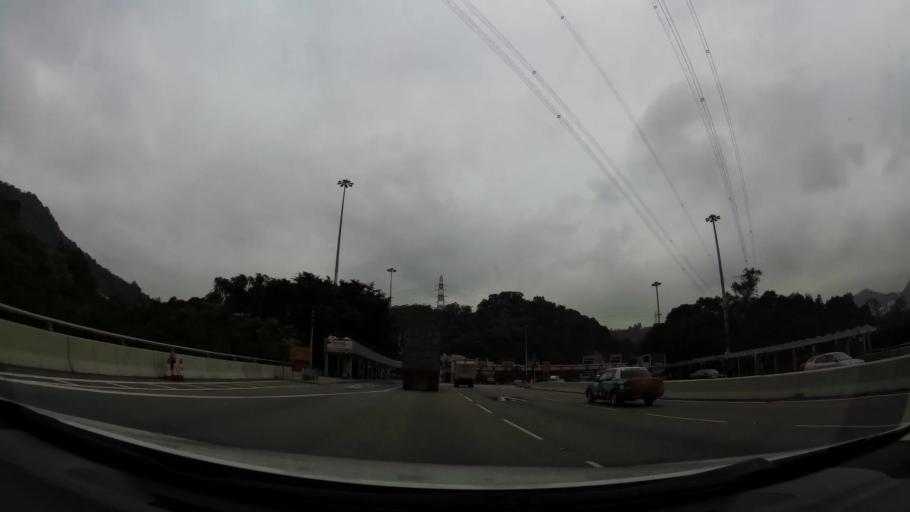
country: HK
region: Tsuen Wan
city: Tsuen Wan
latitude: 22.3818
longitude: 114.1373
